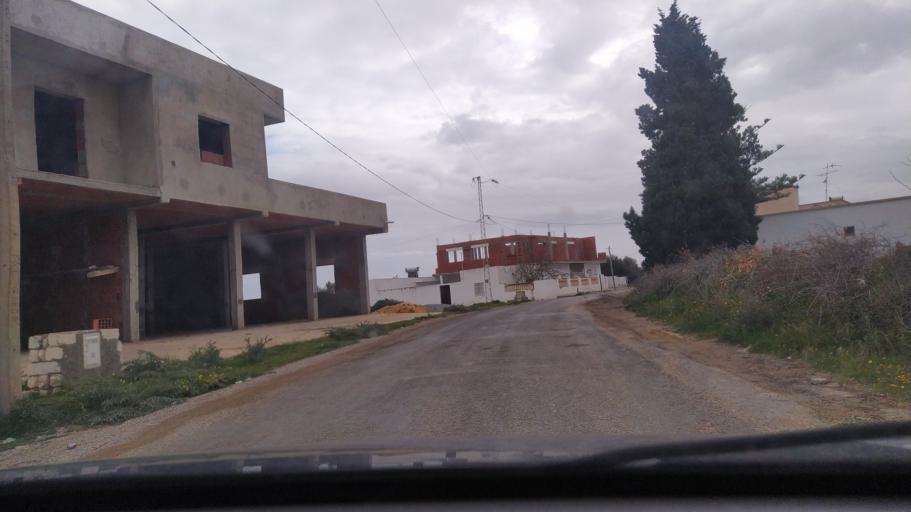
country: TN
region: Al Munastir
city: Sidi Bin Nur
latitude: 35.5146
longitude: 10.9664
